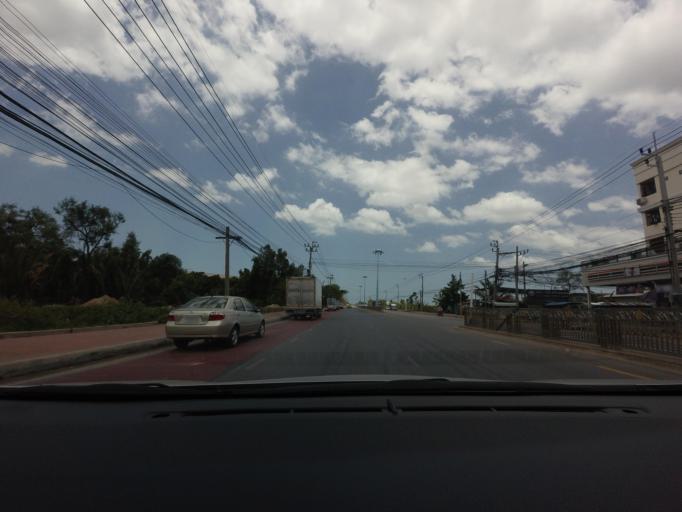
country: TH
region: Samut Prakan
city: Samut Prakan
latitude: 13.5624
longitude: 100.5902
